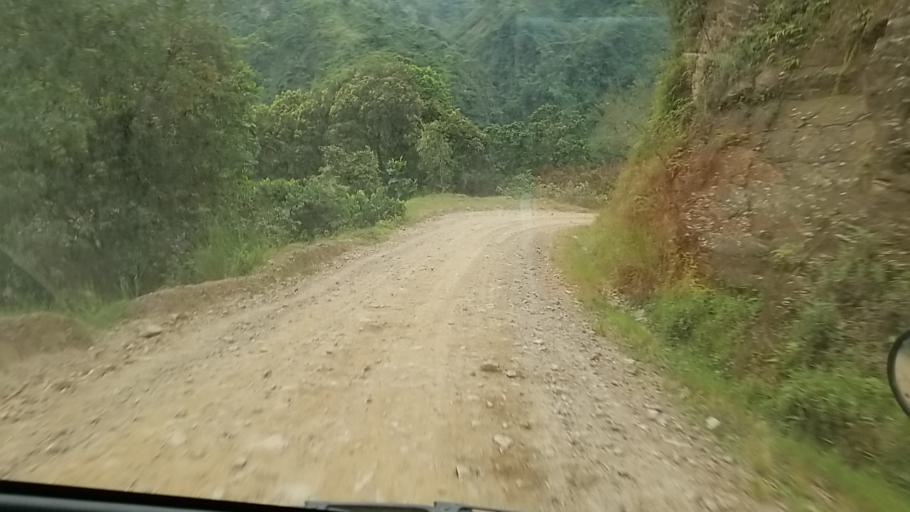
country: CD
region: Nord Kivu
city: Sake
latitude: -1.9652
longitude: 28.9164
